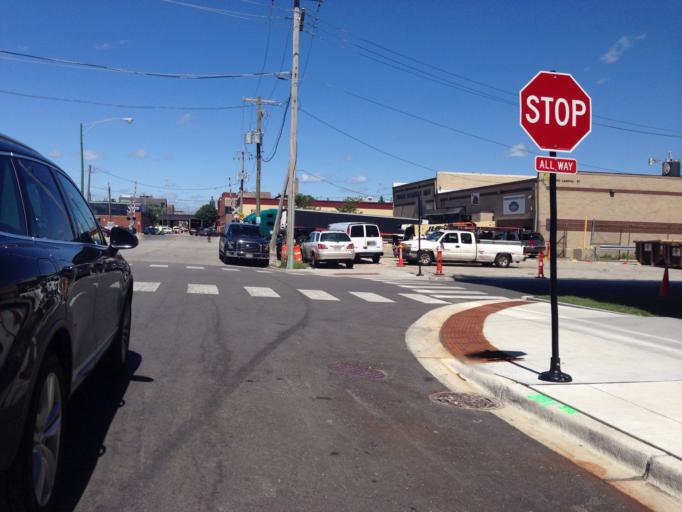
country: US
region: Illinois
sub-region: Cook County
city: Chicago
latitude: 41.8875
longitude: -87.6534
